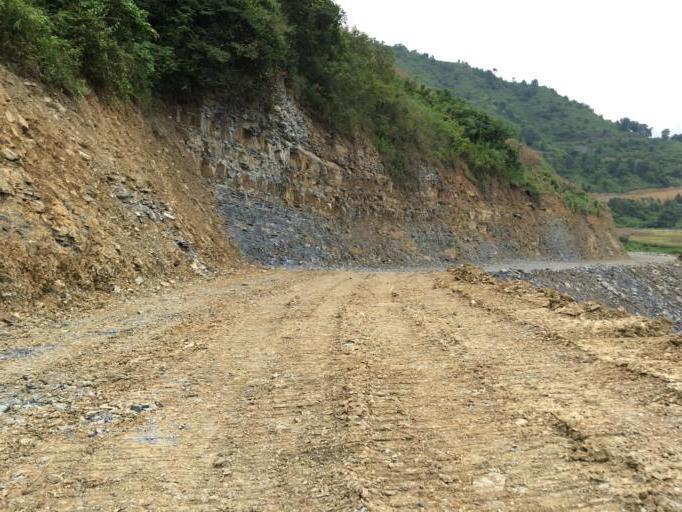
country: CN
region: Guangxi Zhuangzu Zizhiqu
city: Tongle
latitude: 25.1244
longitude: 106.4189
